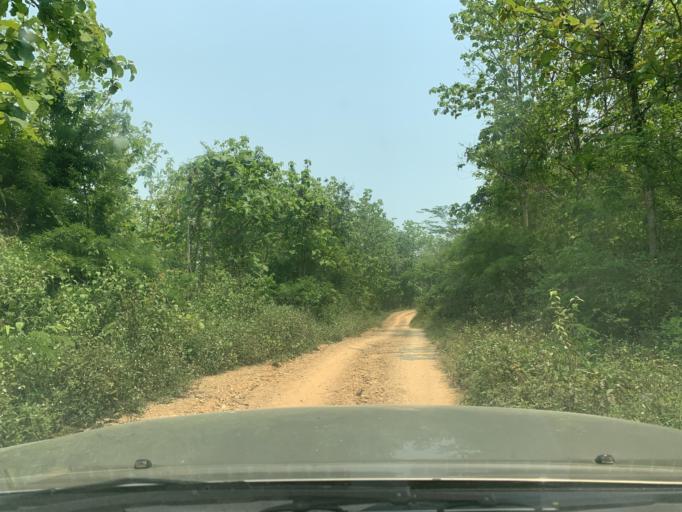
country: LA
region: Louangphabang
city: Xiang Ngeun
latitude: 19.8265
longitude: 102.2154
